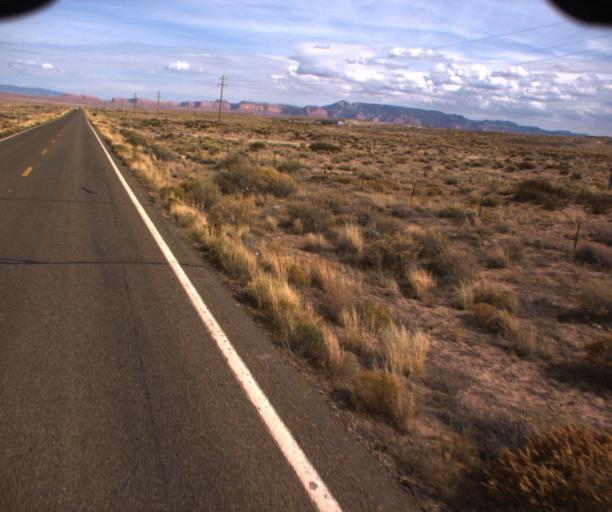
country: US
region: Arizona
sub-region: Apache County
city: Many Farms
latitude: 36.4765
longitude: -109.5150
